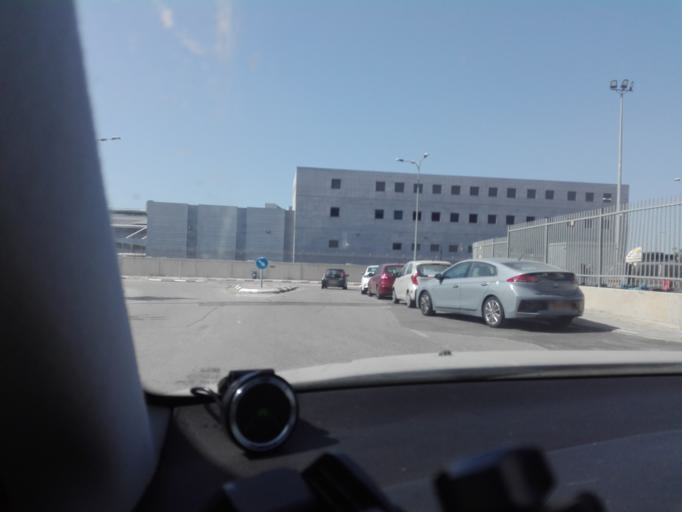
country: IL
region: Central District
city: Bene 'Ayish
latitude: 31.7223
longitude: 34.7624
